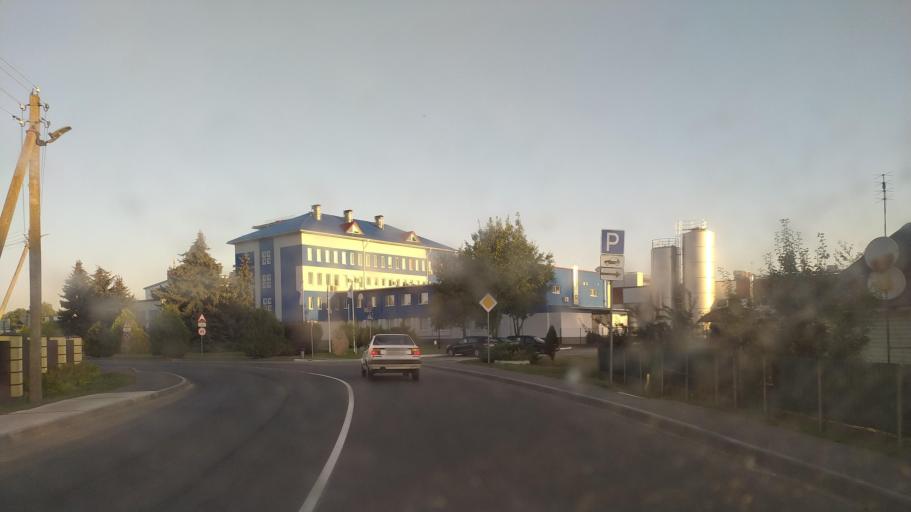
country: BY
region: Brest
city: Byaroza
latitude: 52.5402
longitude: 24.9925
